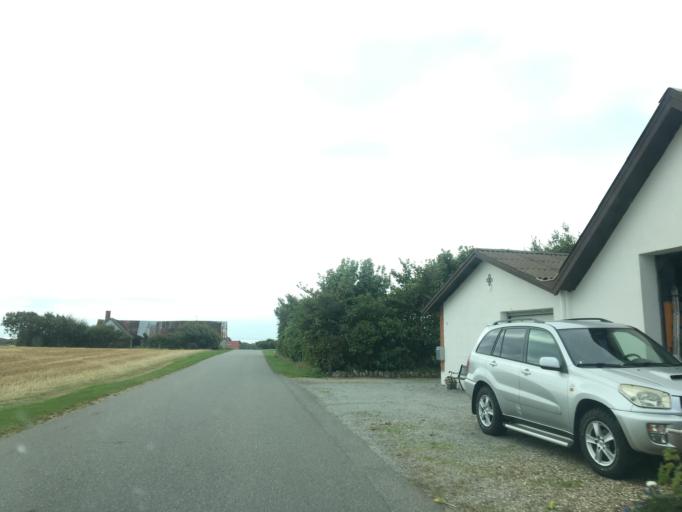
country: DK
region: Central Jutland
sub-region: Lemvig Kommune
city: Thyboron
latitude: 56.7850
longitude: 8.2834
